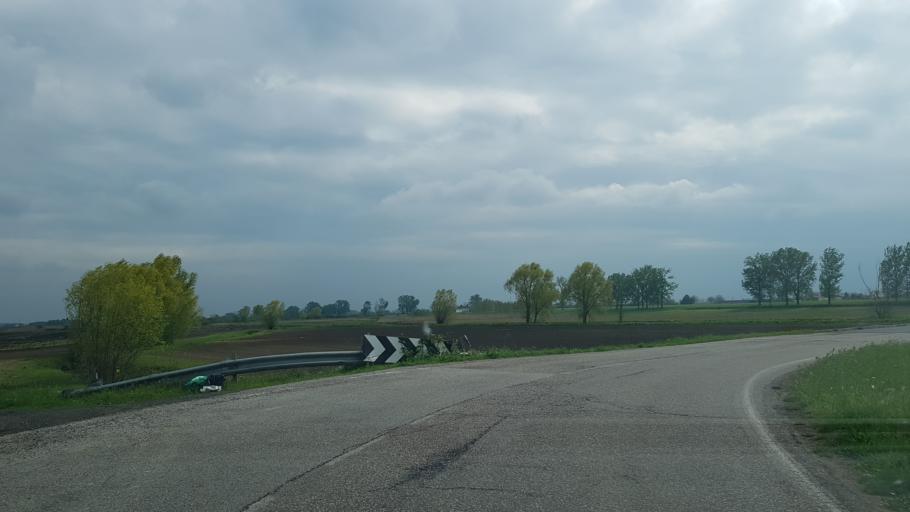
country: IT
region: Veneto
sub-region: Provincia di Verona
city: Maccacari
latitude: 45.1298
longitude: 11.1313
